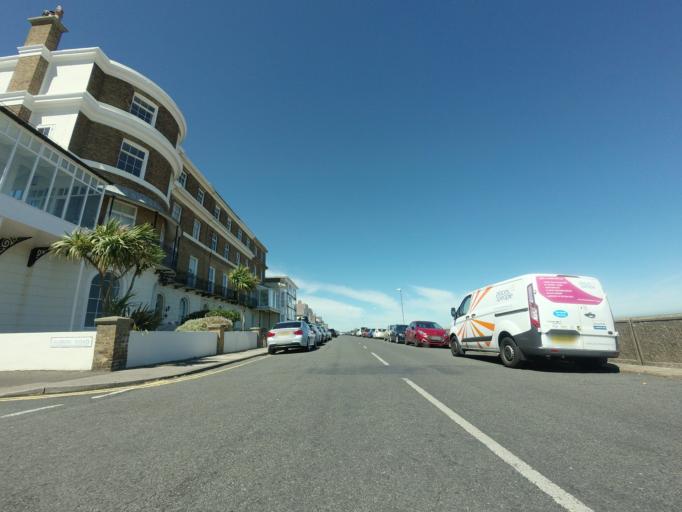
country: GB
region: England
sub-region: Kent
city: Deal
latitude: 51.2324
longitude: 1.4041
